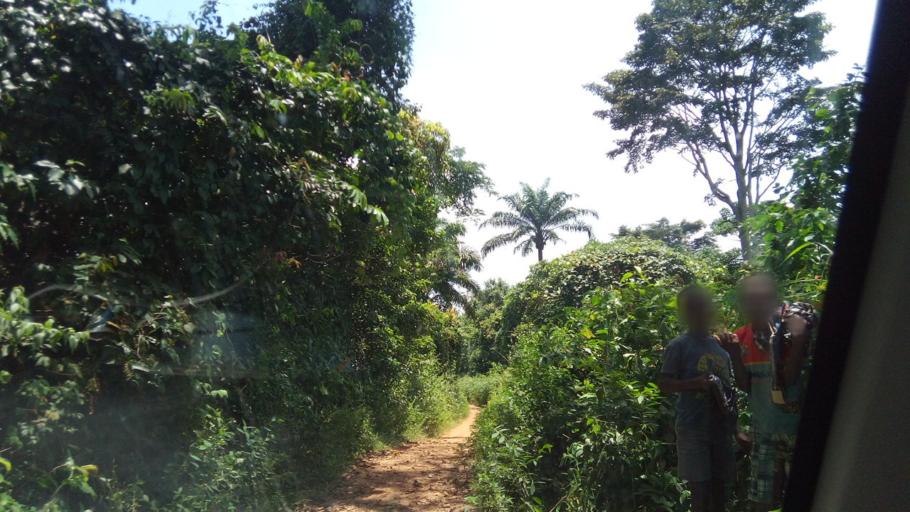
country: AO
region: Zaire
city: Mbanza Congo
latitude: -5.8081
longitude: 14.2446
